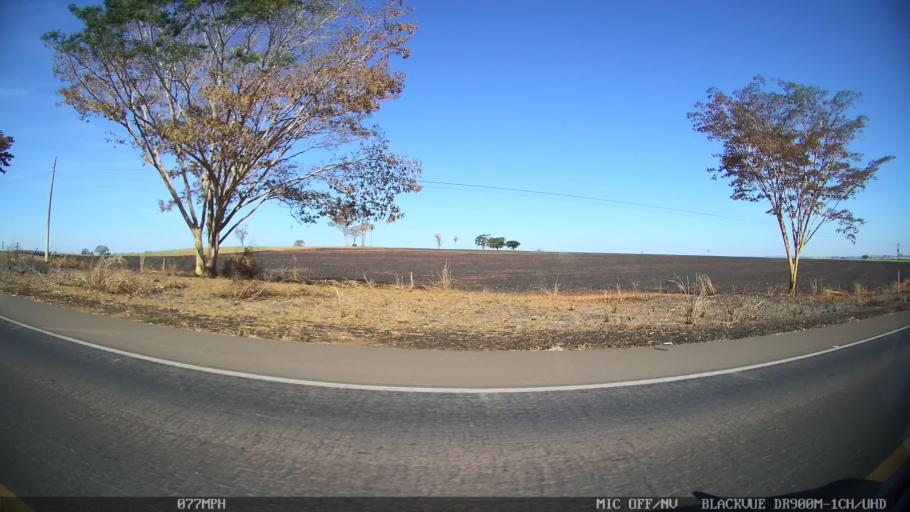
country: BR
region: Sao Paulo
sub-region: Olimpia
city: Olimpia
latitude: -20.6631
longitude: -48.8633
